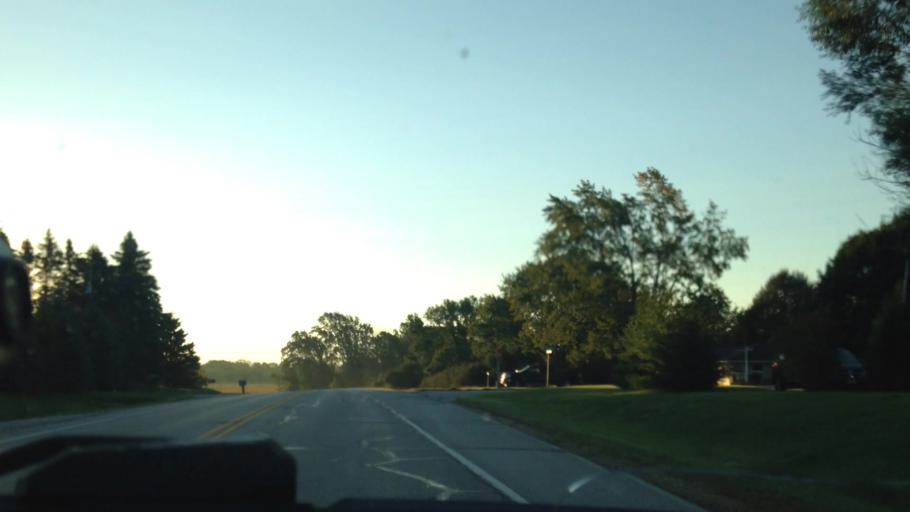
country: US
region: Wisconsin
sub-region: Washington County
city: Newburg
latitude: 43.4236
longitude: -88.0746
